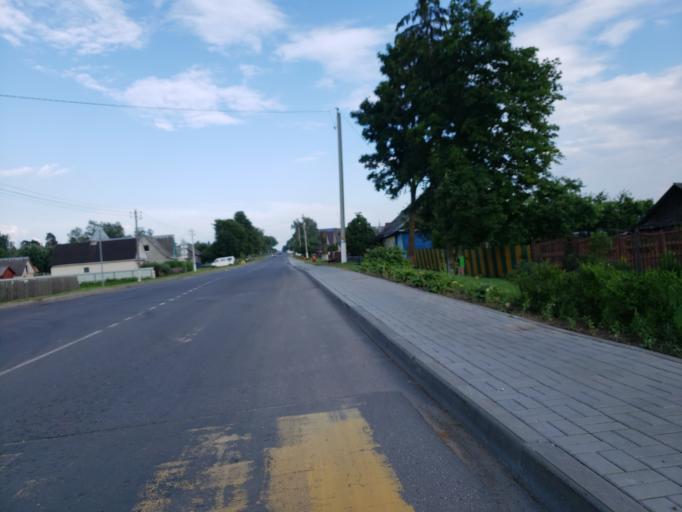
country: BY
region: Minsk
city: Chervyen'
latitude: 53.7078
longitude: 28.4308
